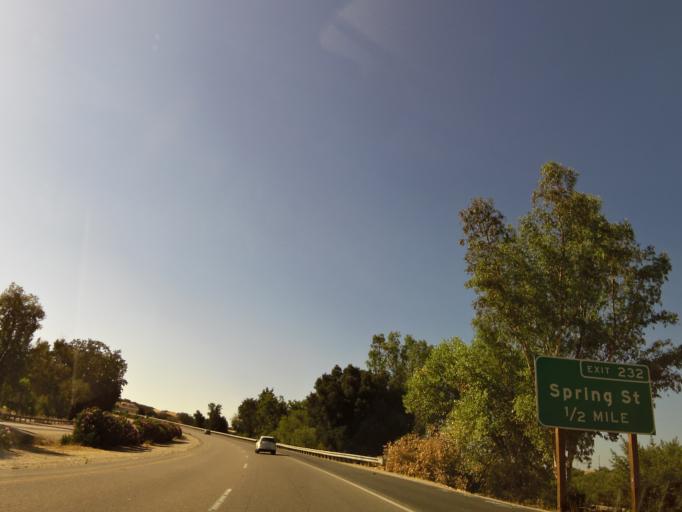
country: US
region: California
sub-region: San Luis Obispo County
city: Paso Robles
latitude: 35.6508
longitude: -120.6896
